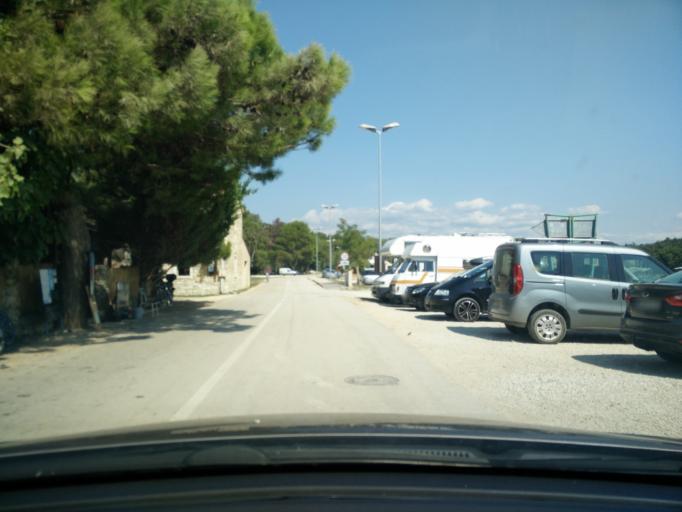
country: HR
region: Istarska
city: Novigrad
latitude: 45.2834
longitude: 13.5972
